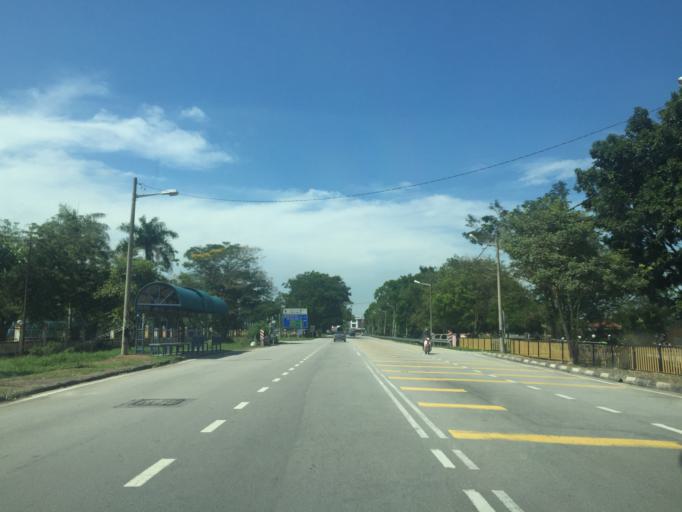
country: MY
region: Penang
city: Tasek Glugor
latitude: 5.4889
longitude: 100.4610
